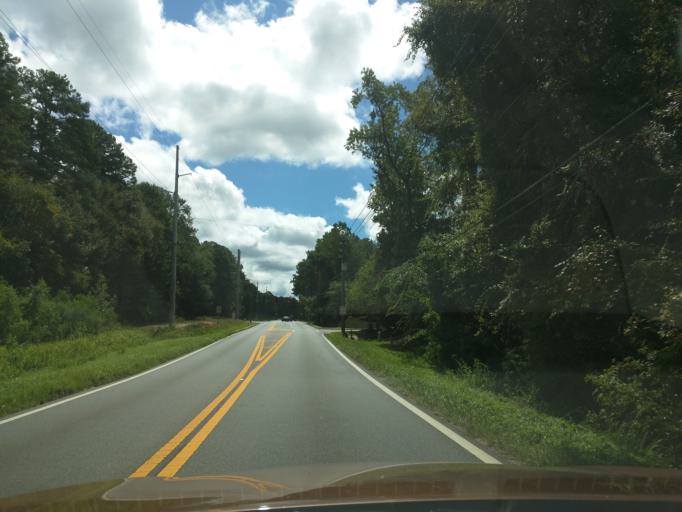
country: US
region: Florida
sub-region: Leon County
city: Tallahassee
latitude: 30.5795
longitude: -84.2384
